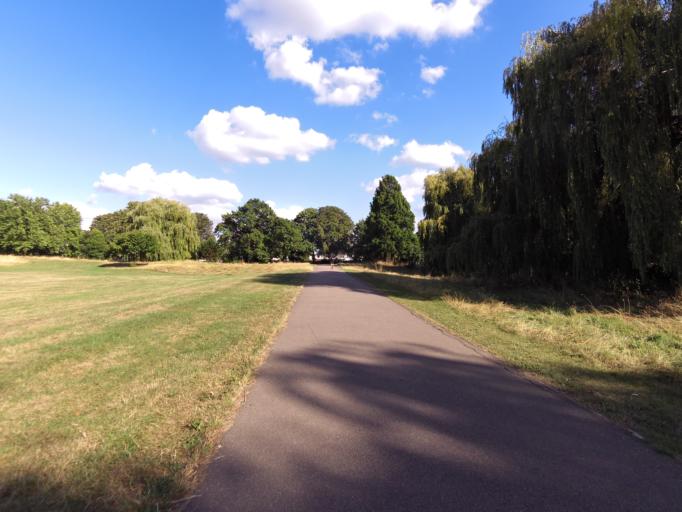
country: GB
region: England
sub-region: Greater London
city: Wood Green
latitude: 51.6170
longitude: -0.1273
